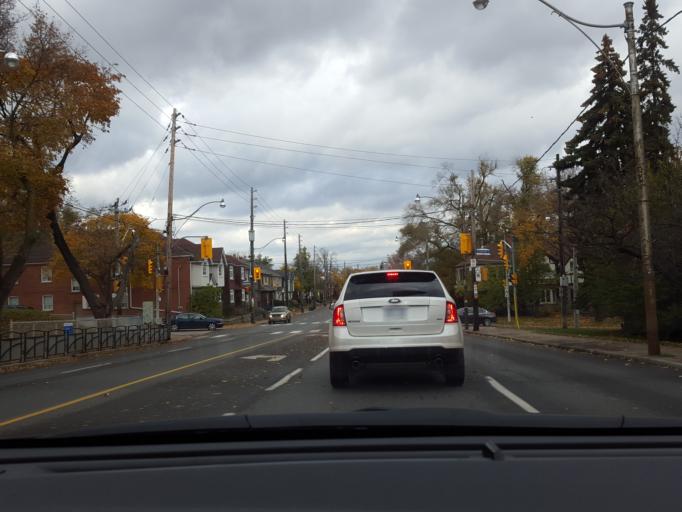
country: CA
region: Ontario
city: Toronto
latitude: 43.7100
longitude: -79.4110
